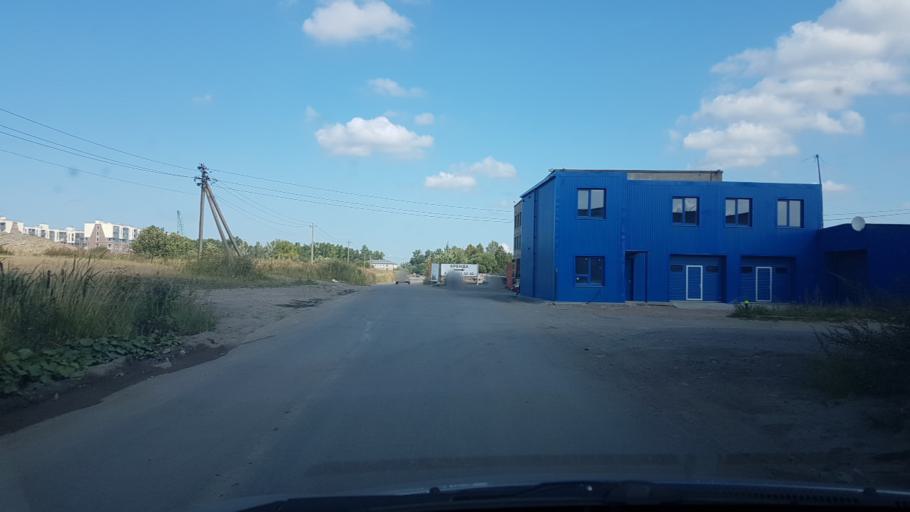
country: RU
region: St.-Petersburg
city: Sosnovaya Polyana
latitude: 59.8416
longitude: 30.1197
